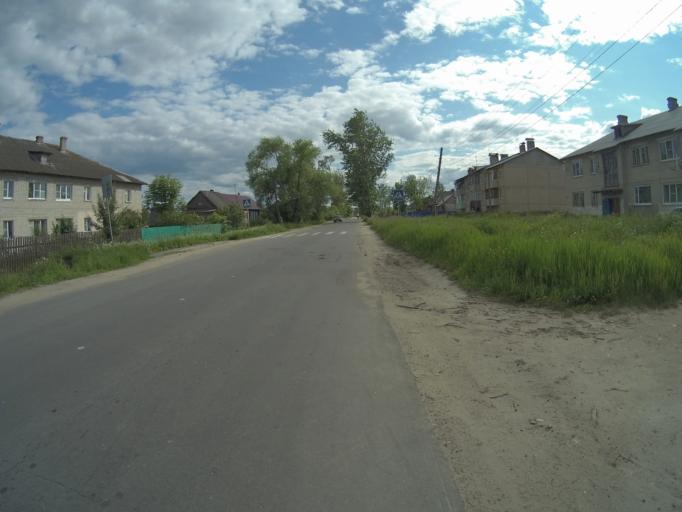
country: RU
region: Vladimir
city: Sudogda
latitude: 55.9389
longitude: 40.8437
